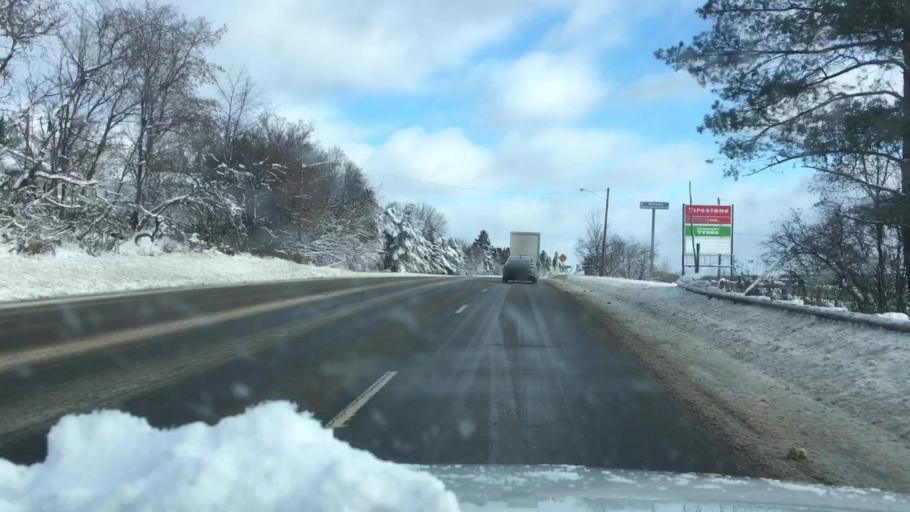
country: US
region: Maine
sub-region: Aroostook County
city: Caribou
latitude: 46.8579
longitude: -68.0051
